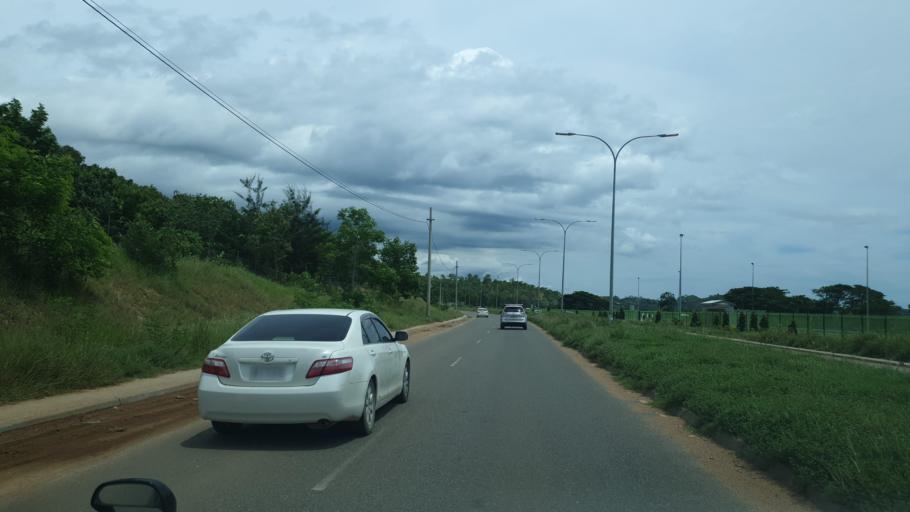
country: PG
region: National Capital
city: Port Moresby
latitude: -9.4951
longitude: 147.2257
